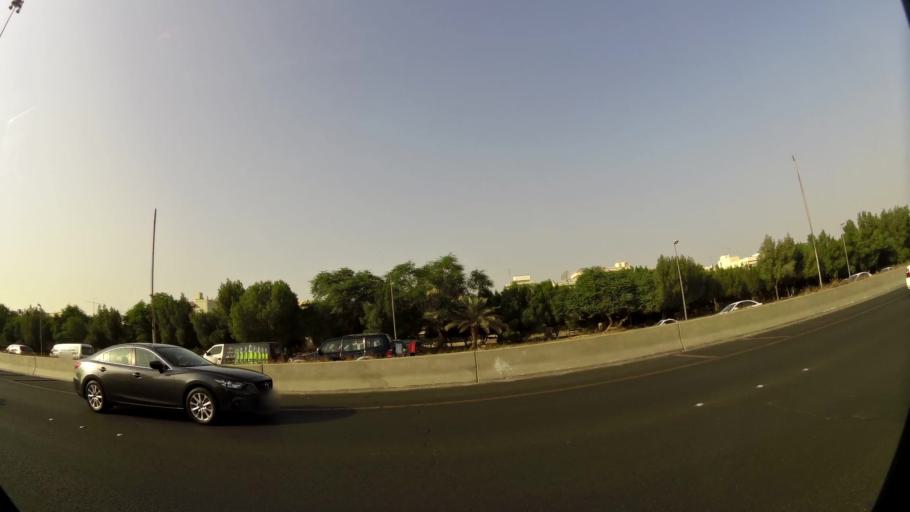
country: KW
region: Muhafazat Hawalli
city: Hawalli
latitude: 29.3056
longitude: 48.0048
